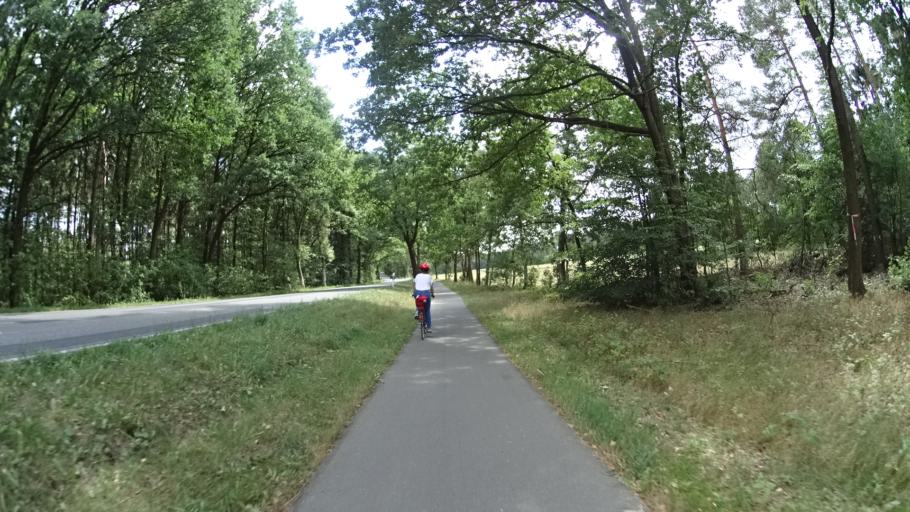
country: DE
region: Lower Saxony
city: Undeloh
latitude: 53.2019
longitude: 9.9643
